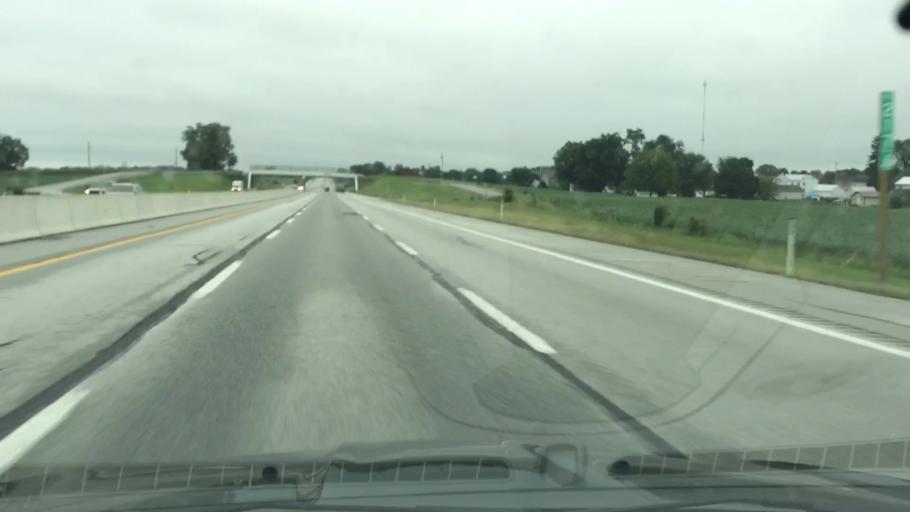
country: US
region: Pennsylvania
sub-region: Cumberland County
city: Newville
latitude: 40.2047
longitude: -77.3170
